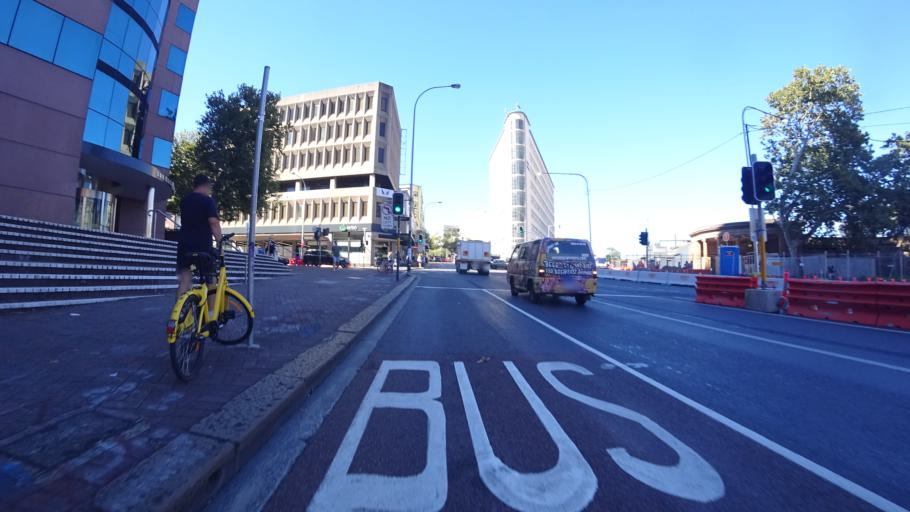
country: AU
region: New South Wales
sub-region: City of Sydney
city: Haymarket
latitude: -33.8832
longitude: 151.2085
